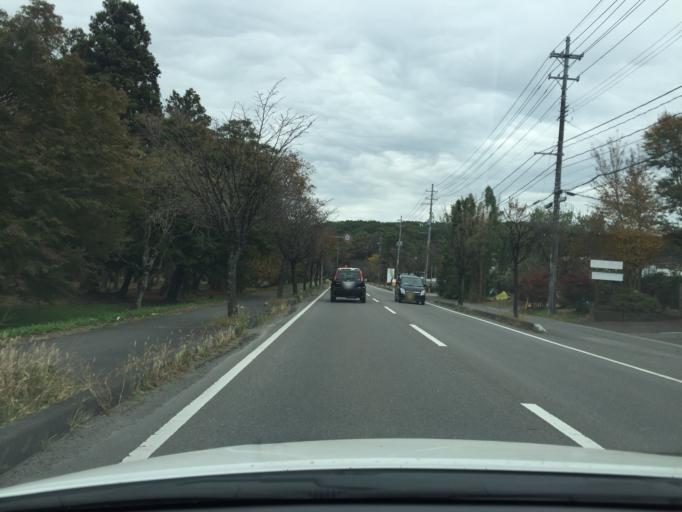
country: JP
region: Tochigi
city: Kuroiso
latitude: 37.1085
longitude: 140.2128
